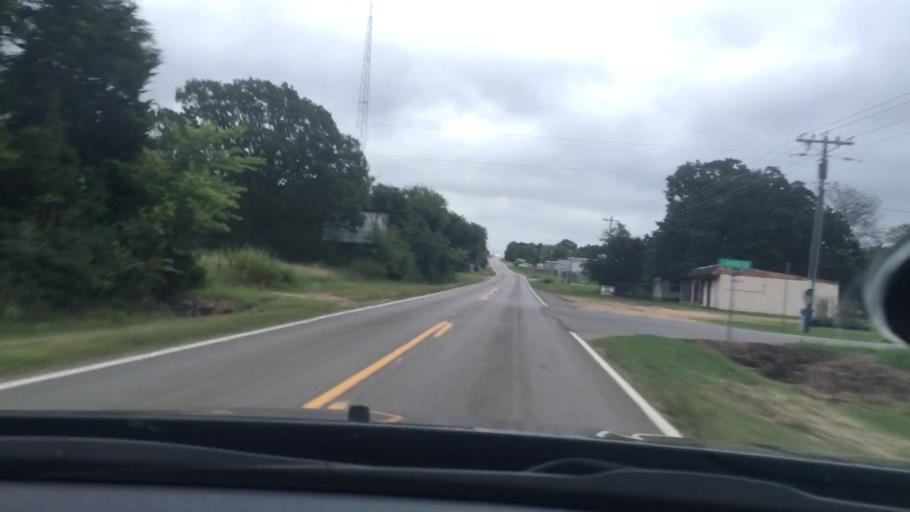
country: US
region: Oklahoma
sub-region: Sequoyah County
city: Vian
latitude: 35.6024
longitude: -95.0212
